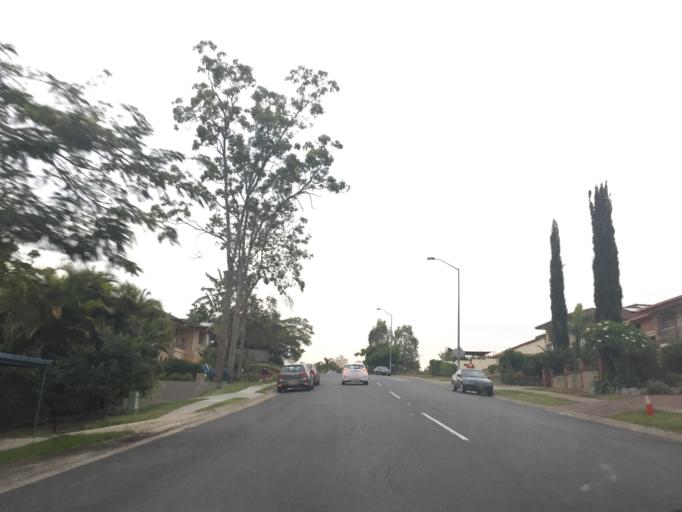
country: AU
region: Queensland
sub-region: Moreton Bay
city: Ferny Hills
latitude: -27.4425
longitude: 152.9382
